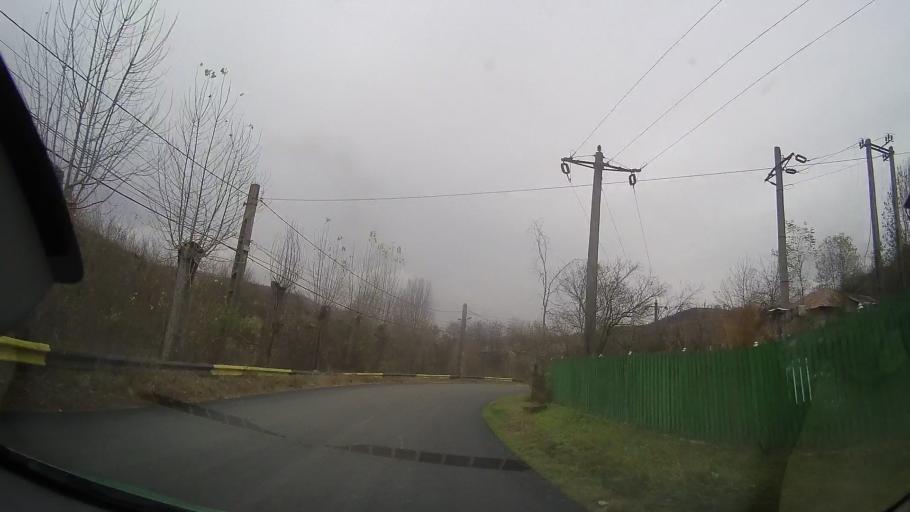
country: RO
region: Prahova
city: Ceptura de Sus
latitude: 45.0480
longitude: 26.3026
